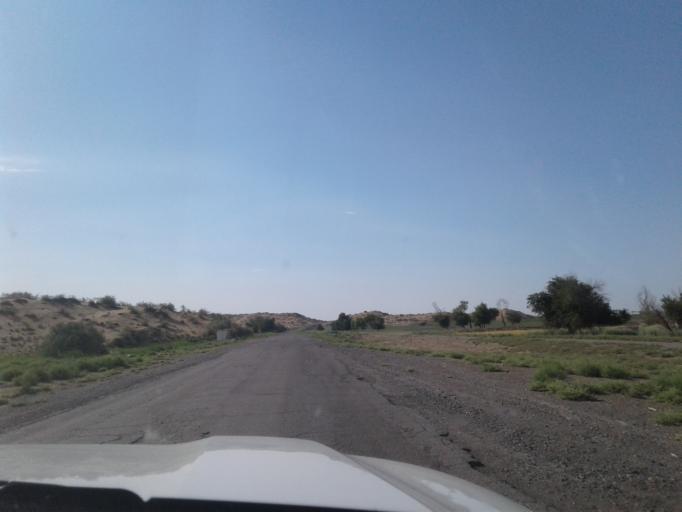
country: TM
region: Mary
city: Yoloeten
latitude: 36.6859
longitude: 62.4680
